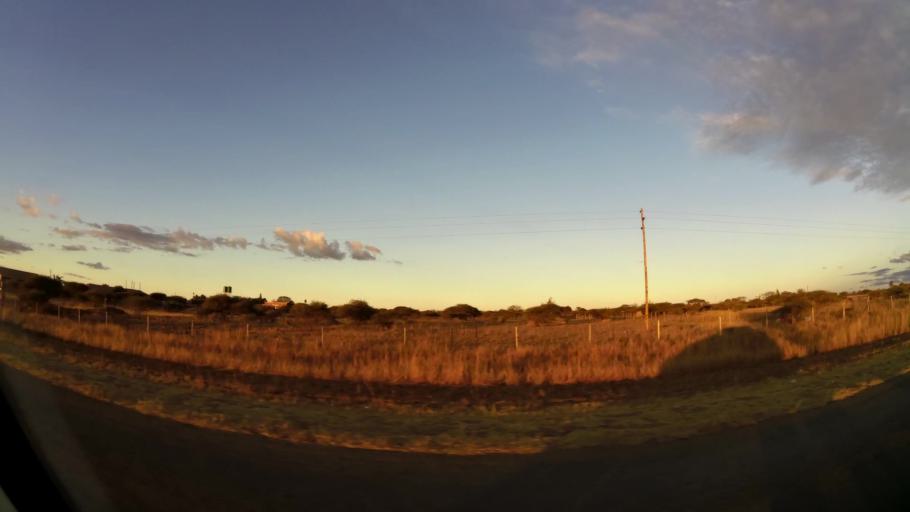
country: ZA
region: Limpopo
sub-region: Capricorn District Municipality
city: Polokwane
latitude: -23.8087
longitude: 29.4795
